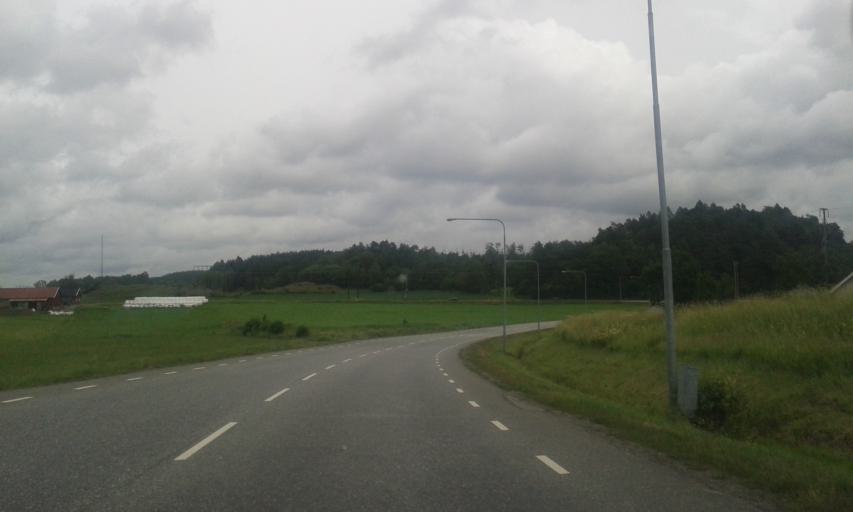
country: SE
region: Vaestra Goetaland
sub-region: Kungalvs Kommun
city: Kungalv
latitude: 57.8700
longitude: 11.9045
